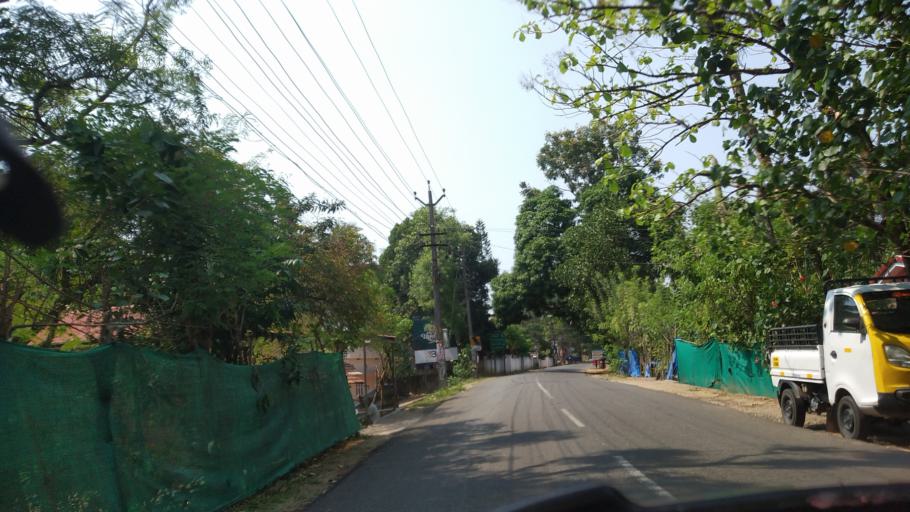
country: IN
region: Kerala
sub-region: Thrissur District
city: Thanniyam
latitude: 10.3399
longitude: 76.1175
